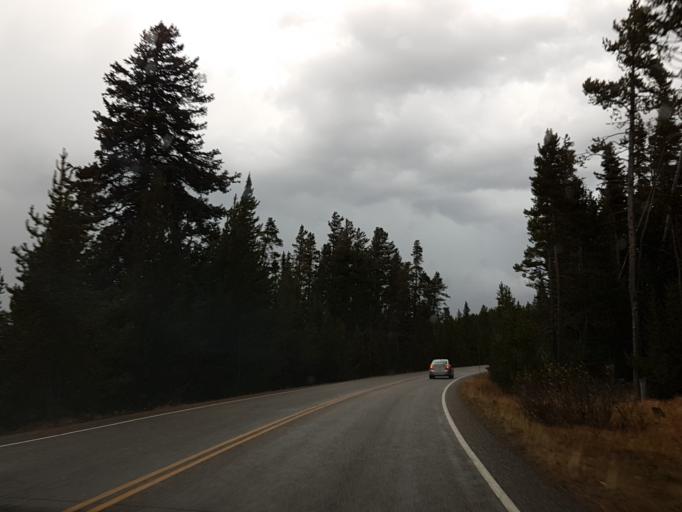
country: US
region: Montana
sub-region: Gallatin County
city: West Yellowstone
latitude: 44.4552
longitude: -110.5074
